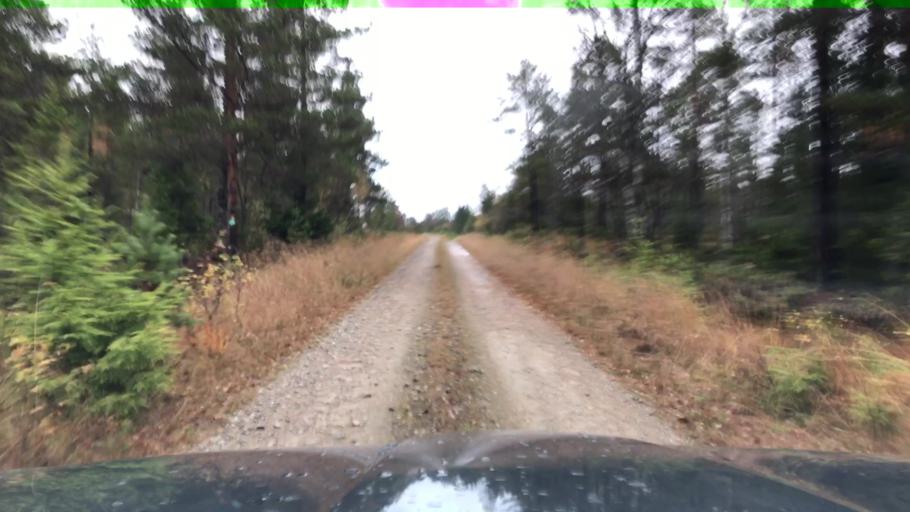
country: NO
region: Hedmark
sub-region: Trysil
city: Innbygda
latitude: 60.9281
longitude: 12.6462
